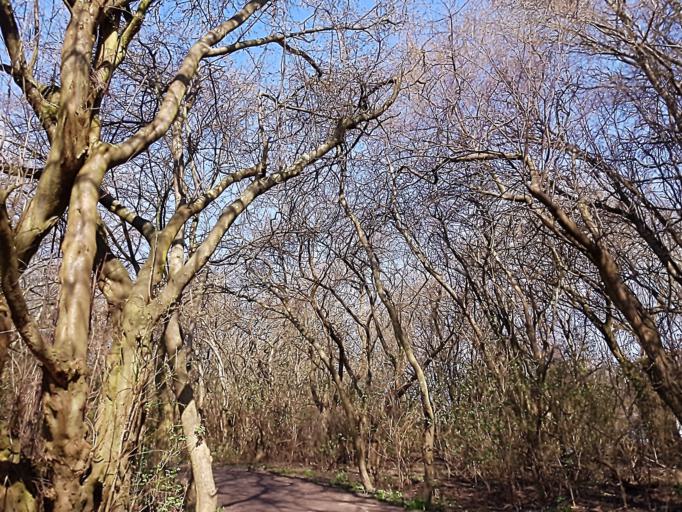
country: DK
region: Capital Region
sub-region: Frederiksberg Kommune
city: Frederiksberg
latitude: 55.6435
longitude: 12.5300
